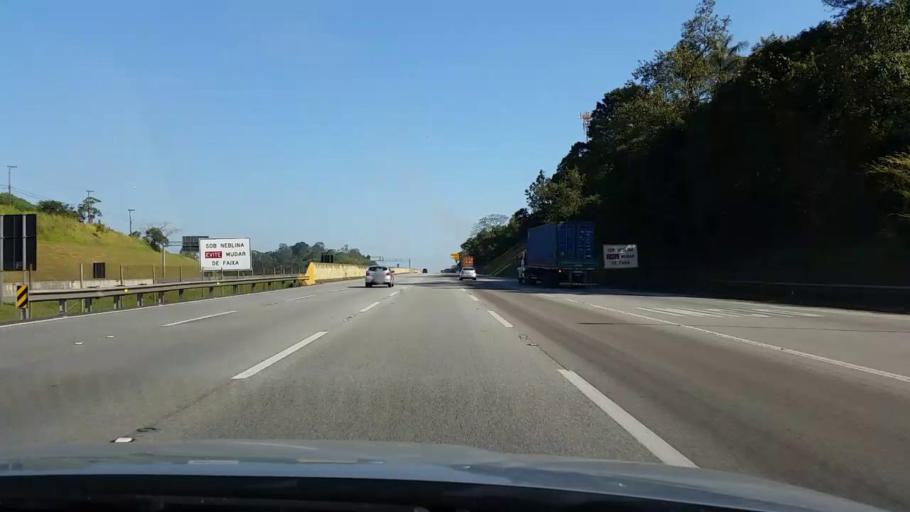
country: BR
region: Sao Paulo
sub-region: Sao Bernardo Do Campo
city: Sao Bernardo do Campo
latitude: -23.7735
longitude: -46.5943
